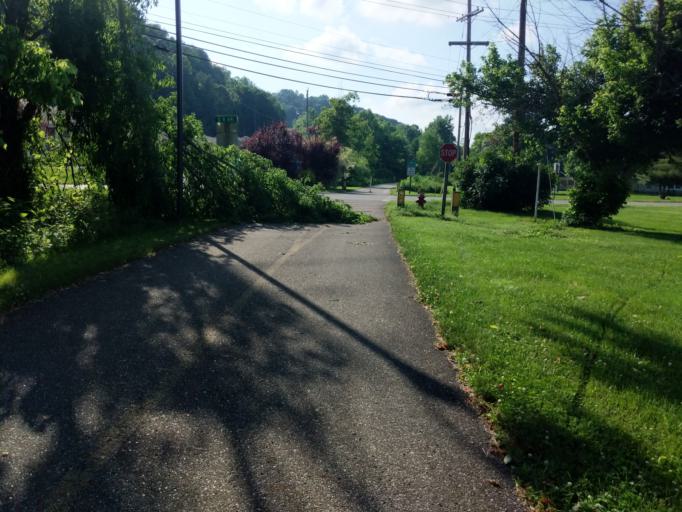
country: US
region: Ohio
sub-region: Athens County
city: Nelsonville
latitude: 39.4327
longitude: -82.2123
